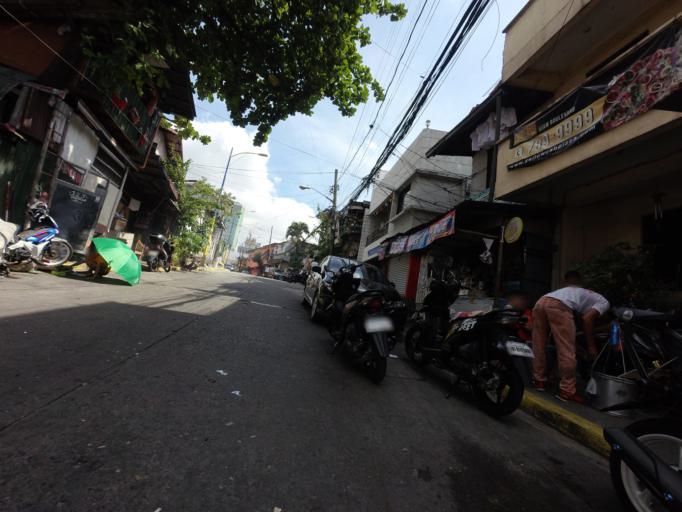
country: PH
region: Metro Manila
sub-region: Mandaluyong
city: Mandaluyong City
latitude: 14.5881
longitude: 121.0333
